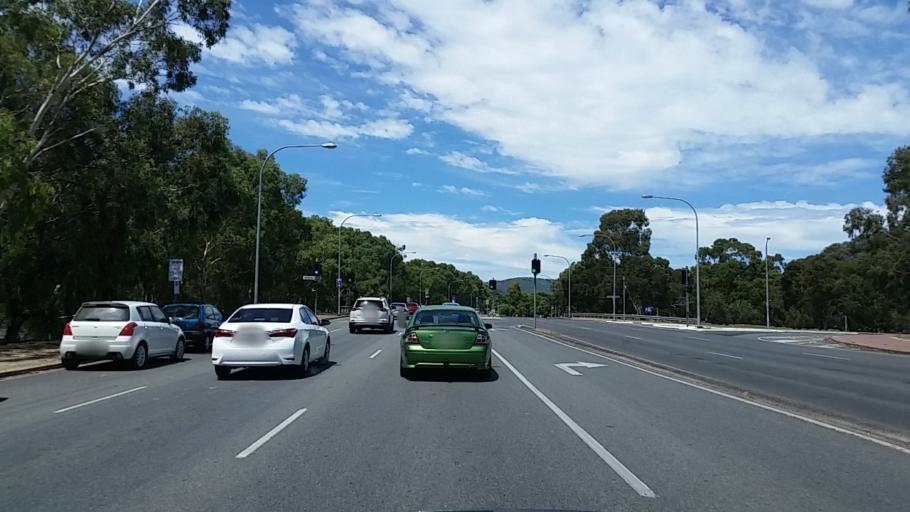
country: AU
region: South Australia
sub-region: Campbelltown
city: Paradise
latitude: -34.8666
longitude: 138.6625
